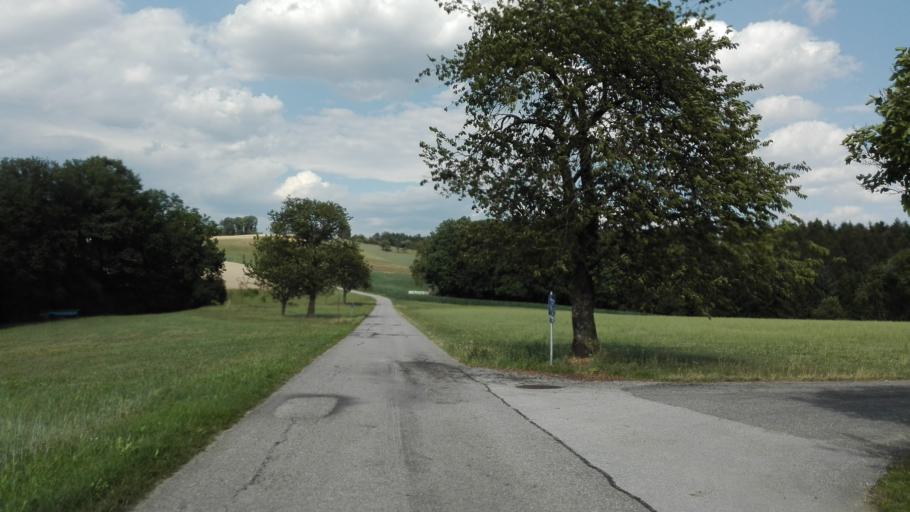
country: AT
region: Upper Austria
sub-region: Politischer Bezirk Perg
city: Perg
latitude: 48.2464
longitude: 14.7053
